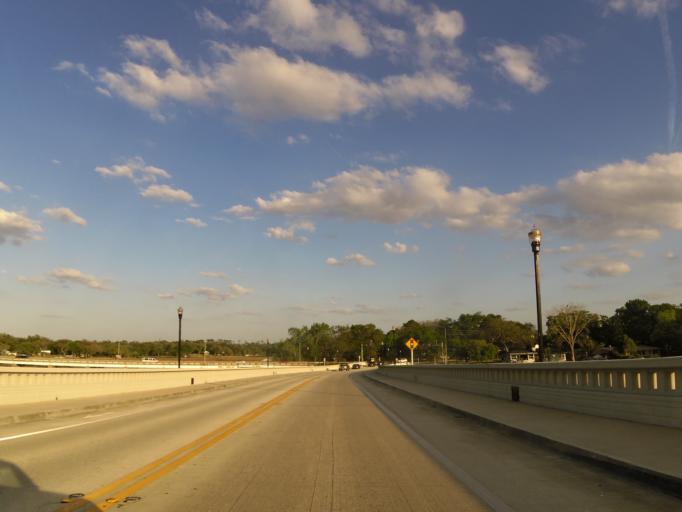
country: US
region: Florida
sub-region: Duval County
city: Jacksonville
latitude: 30.3222
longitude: -81.6000
